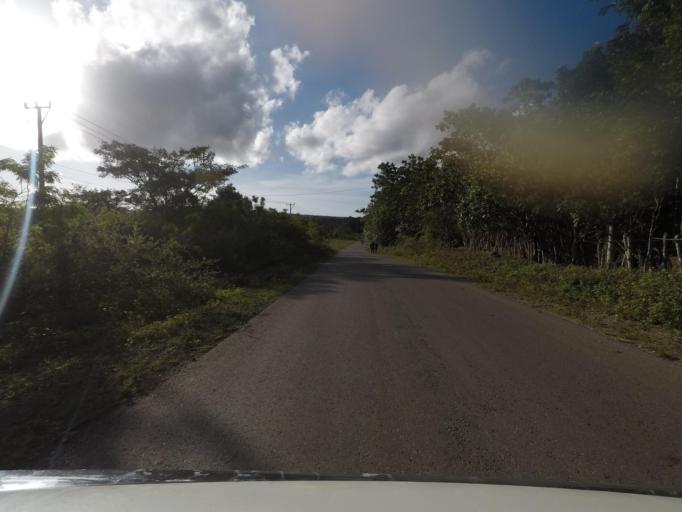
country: TL
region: Lautem
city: Lospalos
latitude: -8.4344
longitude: 127.0046
